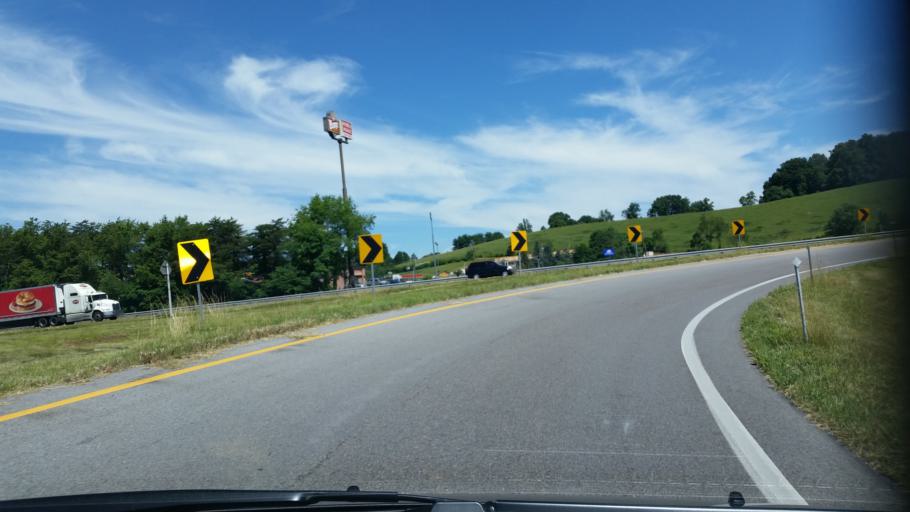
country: US
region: Virginia
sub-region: Washington County
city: Abingdon
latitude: 36.7126
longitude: -81.9349
